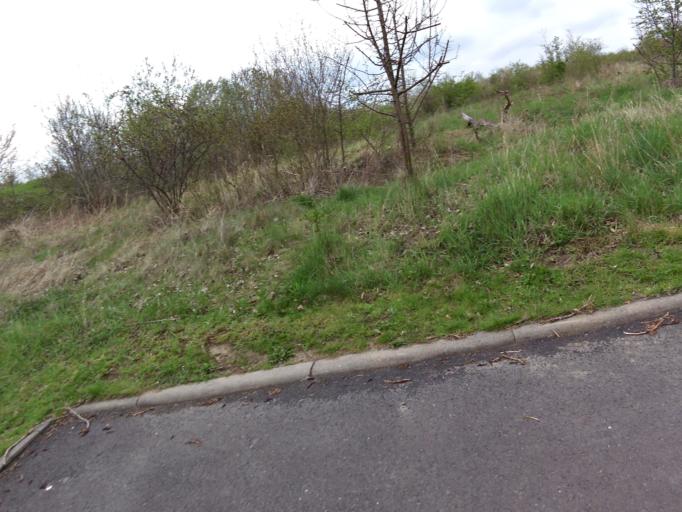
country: DE
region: Thuringia
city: Gotha
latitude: 50.9408
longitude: 10.6727
